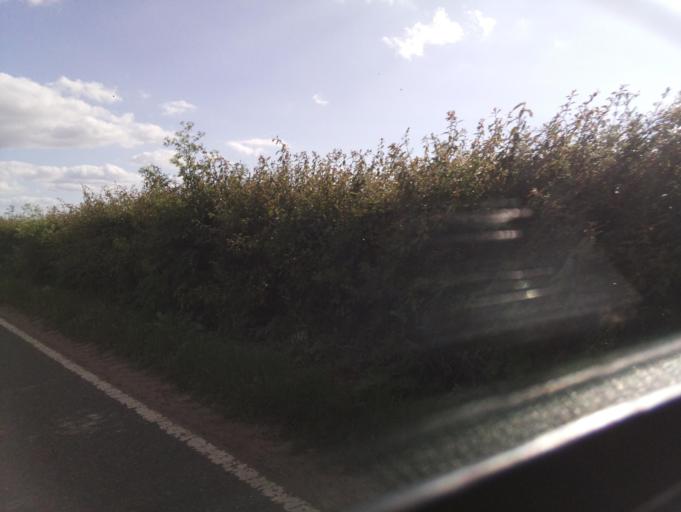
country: GB
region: England
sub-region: Somerset
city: Westonzoyland
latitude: 51.0917
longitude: -2.8776
